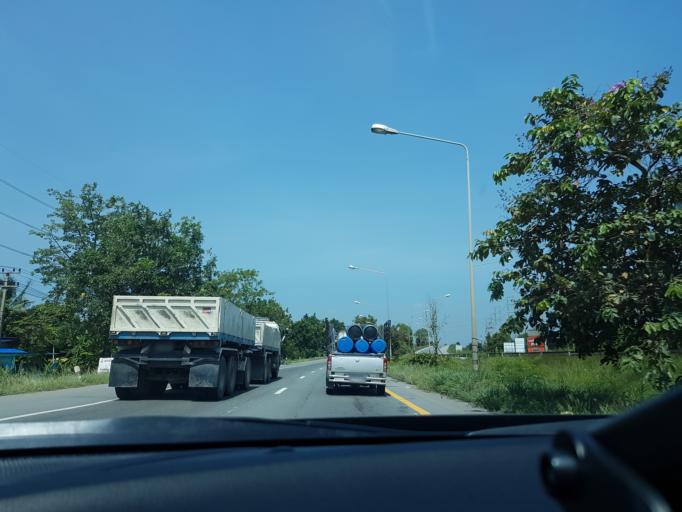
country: TH
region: Sara Buri
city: Saraburi
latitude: 14.5214
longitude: 100.8897
